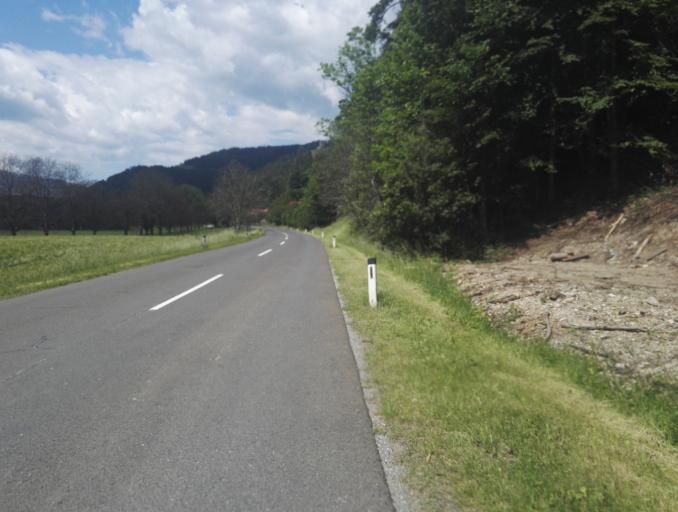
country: AT
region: Styria
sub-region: Politischer Bezirk Graz-Umgebung
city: Frohnleiten
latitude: 47.2221
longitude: 15.3011
